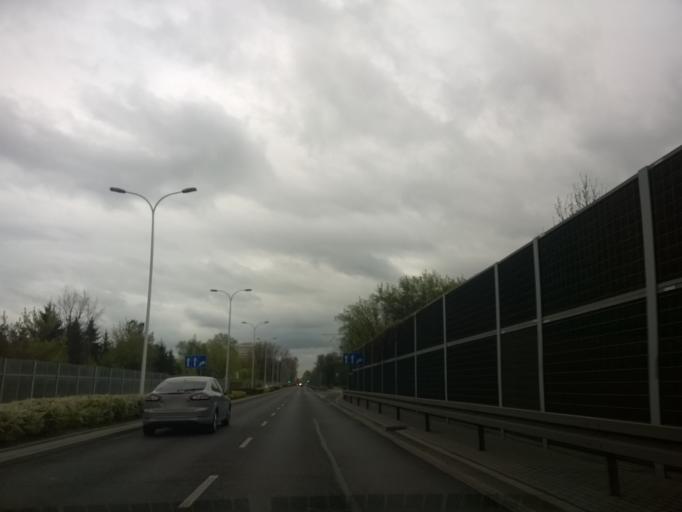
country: PL
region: Masovian Voivodeship
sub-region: Warszawa
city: Ursynow
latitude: 52.1721
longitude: 21.0573
